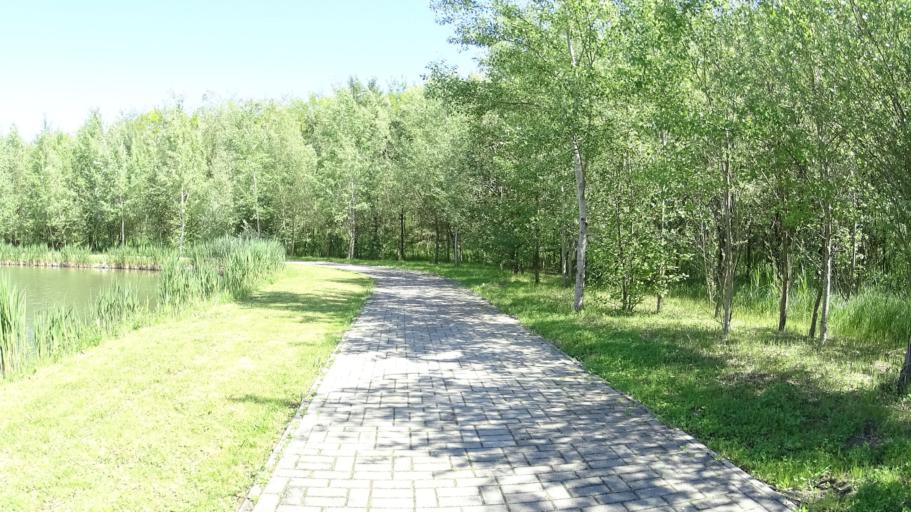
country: HU
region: Komarom-Esztergom
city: Kesztolc
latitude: 47.6998
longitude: 18.8066
